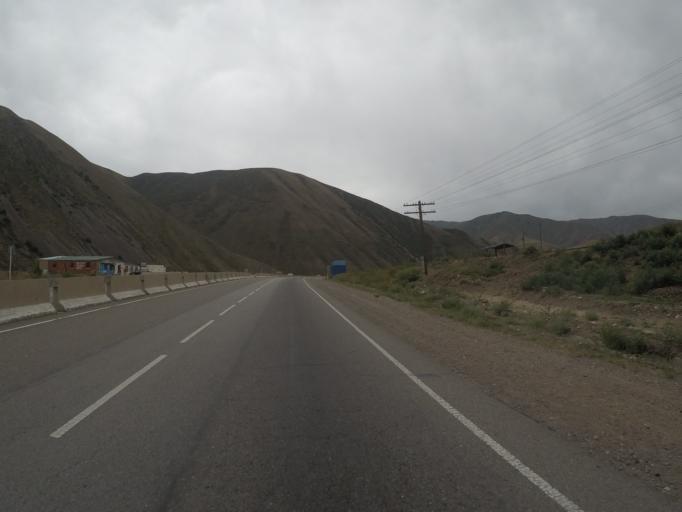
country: KG
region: Chuy
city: Bystrovka
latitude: 42.6800
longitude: 75.8925
